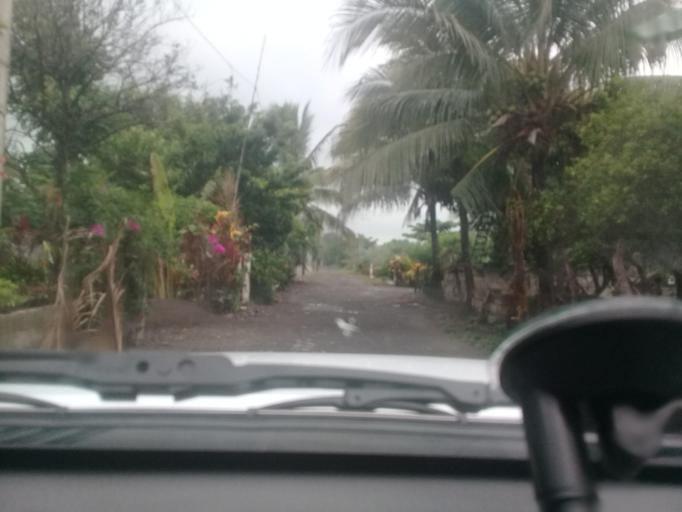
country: MX
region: Veracruz
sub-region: La Antigua
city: Nicolas Blanco (San Pancho)
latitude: 19.3396
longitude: -96.3583
